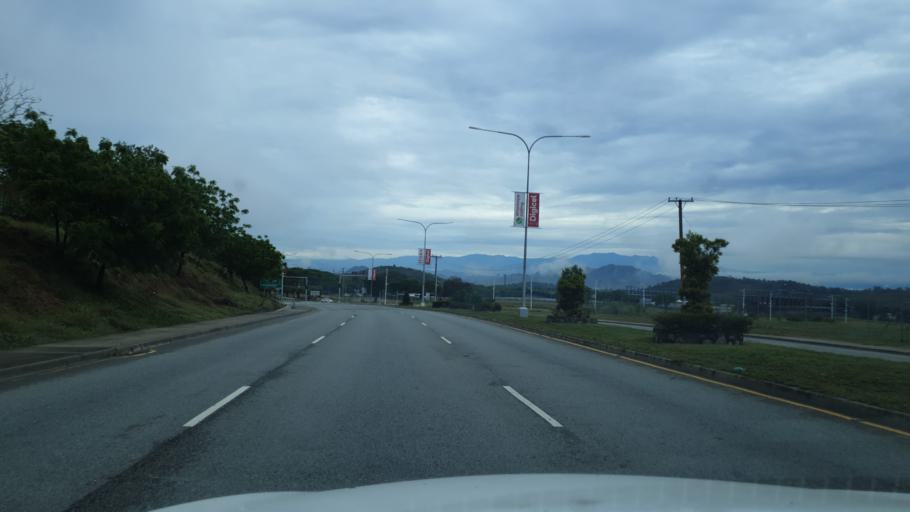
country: PG
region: National Capital
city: Port Moresby
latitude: -9.4298
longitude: 147.1796
